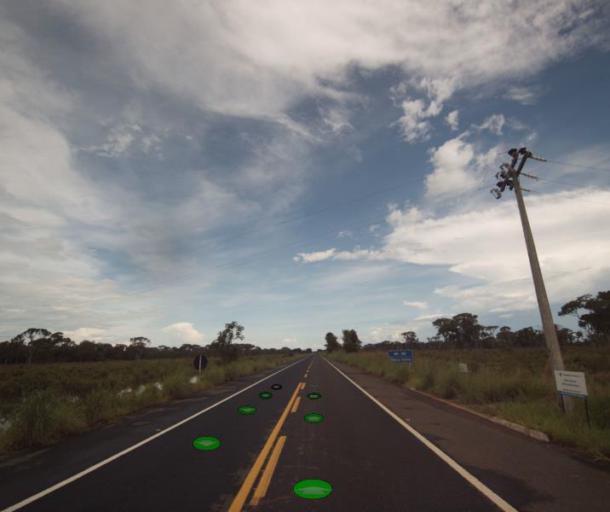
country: BR
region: Goias
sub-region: Sao Miguel Do Araguaia
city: Sao Miguel do Araguaia
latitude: -13.2225
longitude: -50.5712
